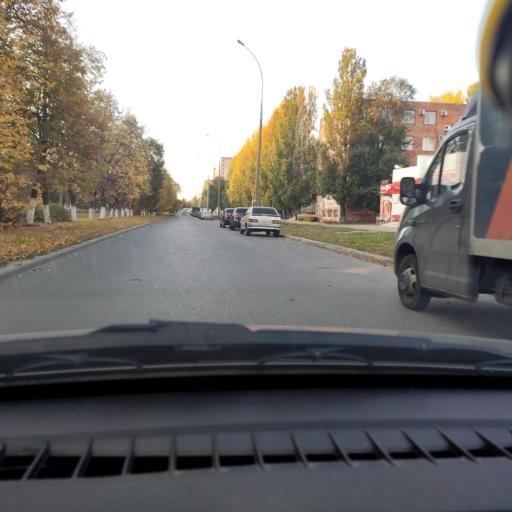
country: RU
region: Samara
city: Tol'yatti
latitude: 53.5315
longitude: 49.3128
